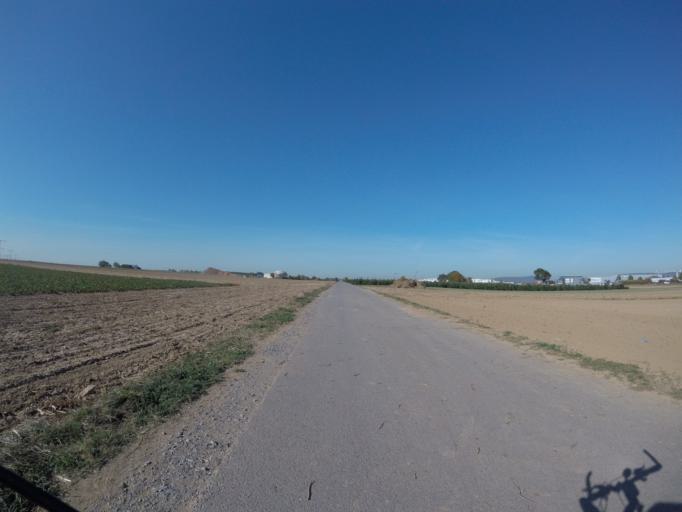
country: DE
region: Baden-Wuerttemberg
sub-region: Regierungsbezirk Stuttgart
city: Bietigheim-Bissingen
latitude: 48.9544
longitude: 9.0837
